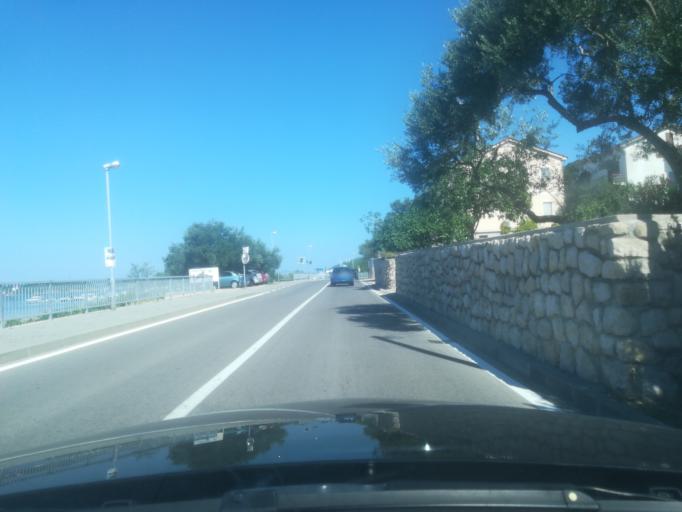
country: HR
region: Primorsko-Goranska
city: Supetarska Draga
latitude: 44.8013
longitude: 14.7289
